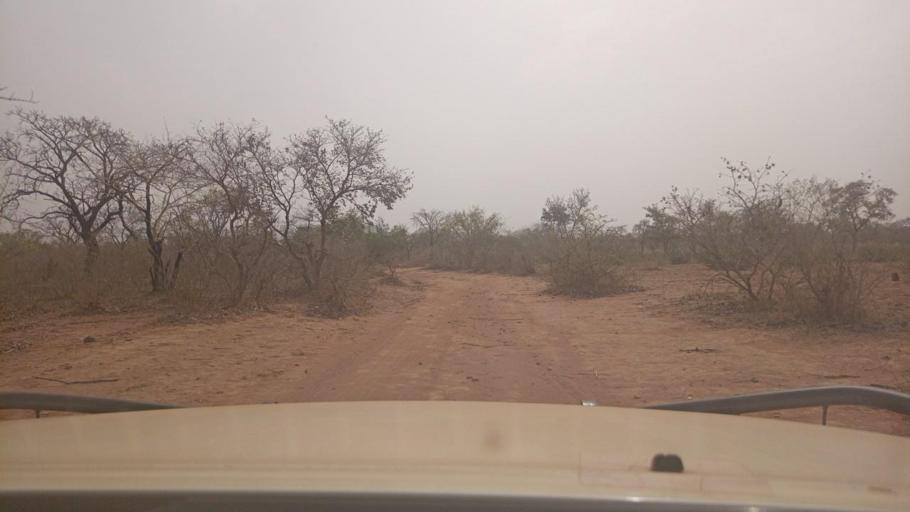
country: BF
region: Boucle du Mouhoun
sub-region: Province des Banwa
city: Salanso
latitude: 12.1605
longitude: -4.2427
